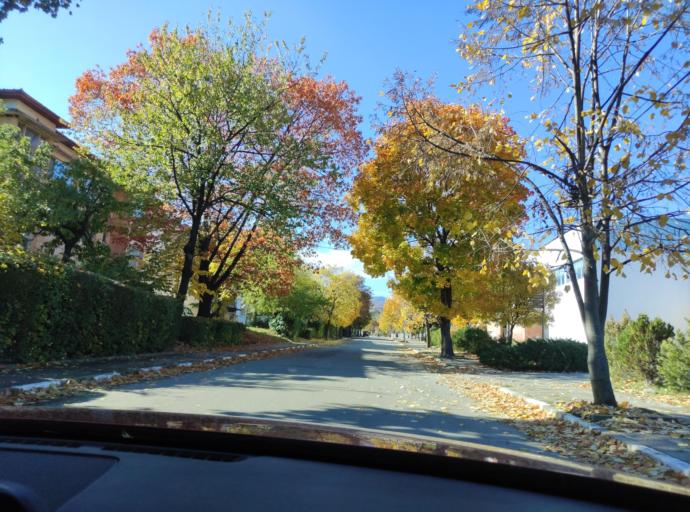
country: BG
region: Montana
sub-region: Obshtina Chiprovtsi
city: Chiprovtsi
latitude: 43.3842
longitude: 22.8875
